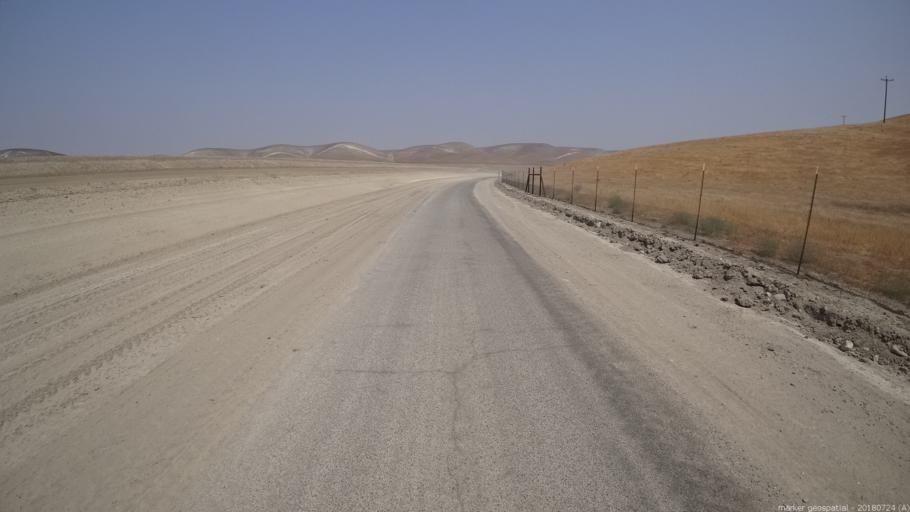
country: US
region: California
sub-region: Monterey County
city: King City
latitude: 36.1964
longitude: -121.0326
